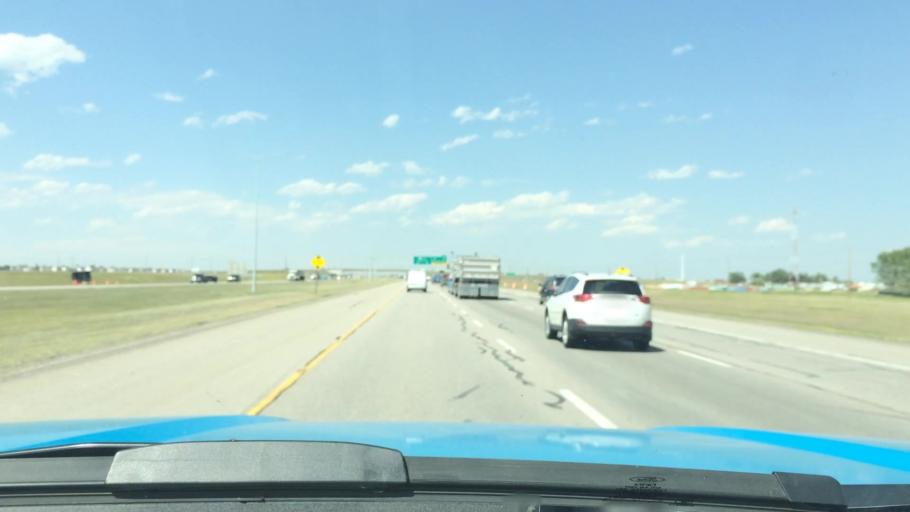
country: CA
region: Alberta
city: Chestermere
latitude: 51.0868
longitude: -113.9193
